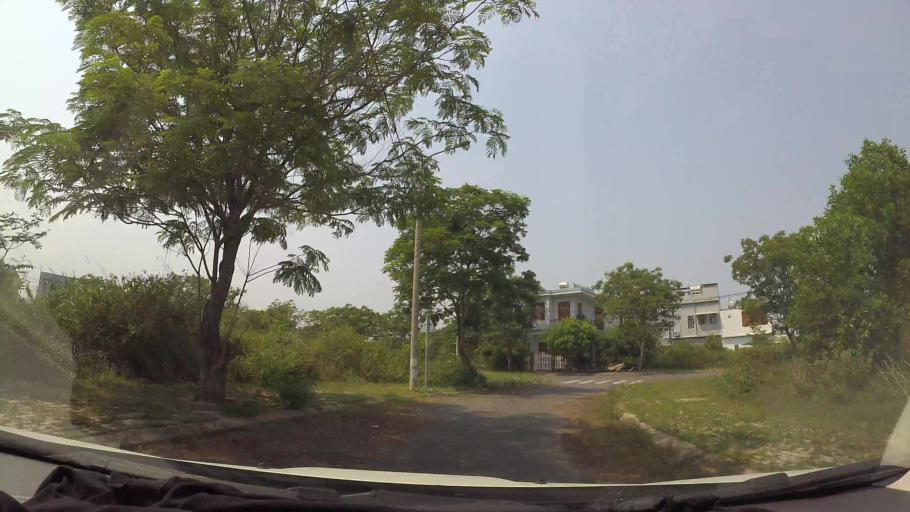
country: VN
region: Da Nang
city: Cam Le
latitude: 15.9918
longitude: 108.2041
